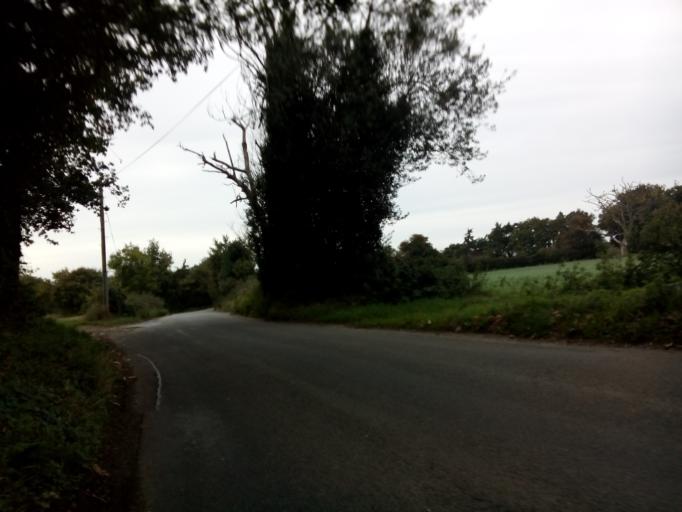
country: GB
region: England
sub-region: Suffolk
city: Ipswich
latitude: 52.0134
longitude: 1.1288
